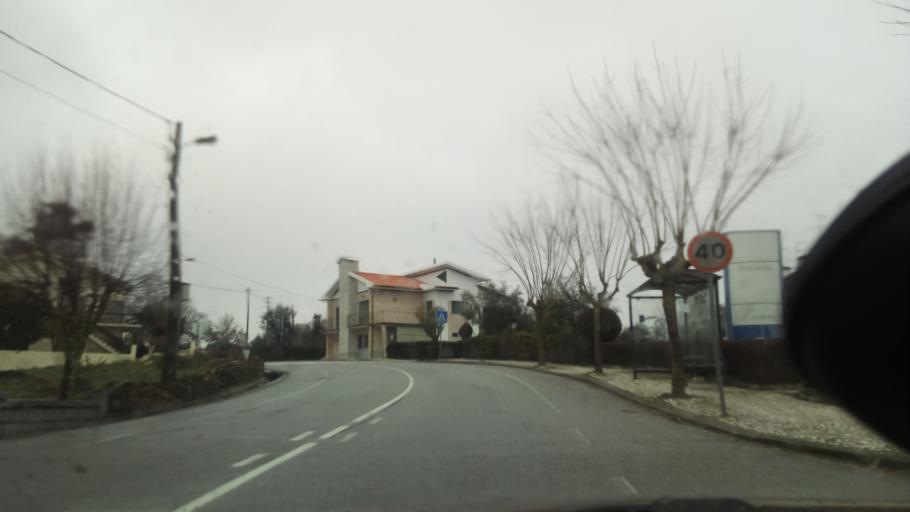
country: PT
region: Viseu
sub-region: Viseu
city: Rio de Loba
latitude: 40.6573
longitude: -7.8729
